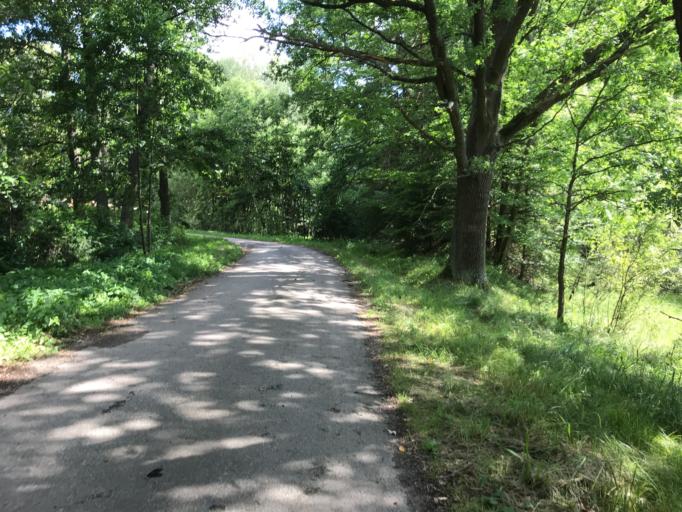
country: CZ
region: Jihocesky
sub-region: Okres Jindrichuv Hradec
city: Trebon
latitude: 48.9899
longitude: 14.7110
